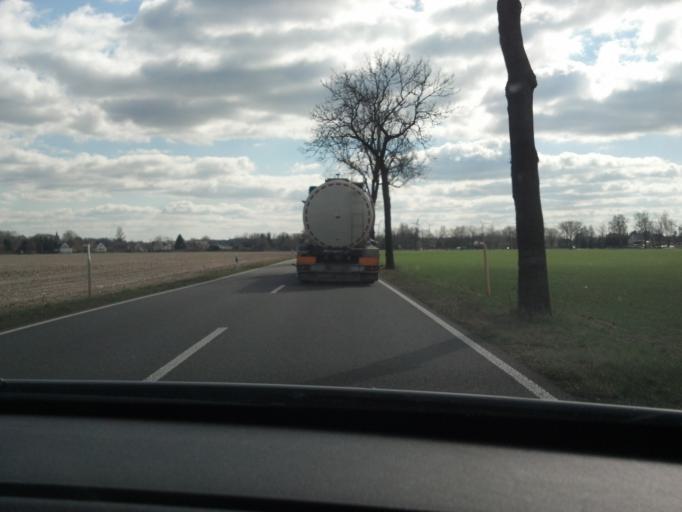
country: DE
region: Brandenburg
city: Gerdshagen
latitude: 53.3284
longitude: 12.2426
